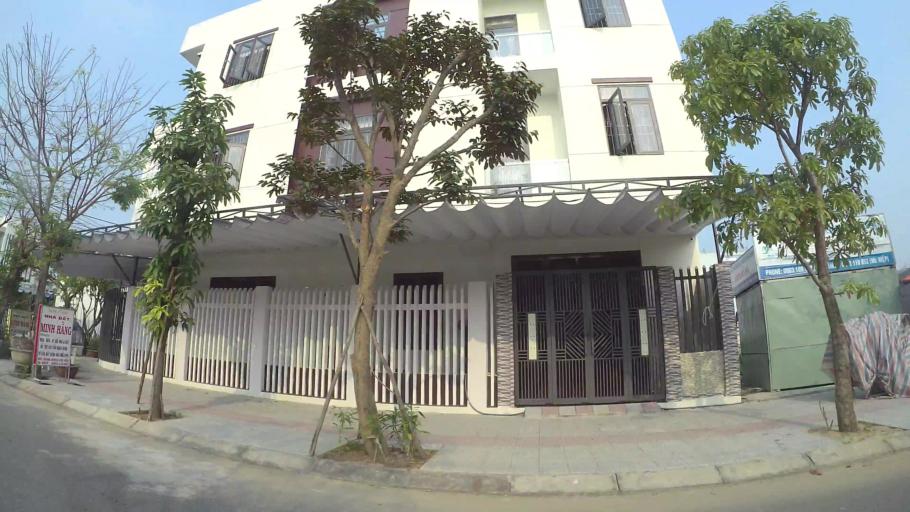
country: VN
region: Da Nang
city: Cam Le
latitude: 16.0056
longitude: 108.2239
